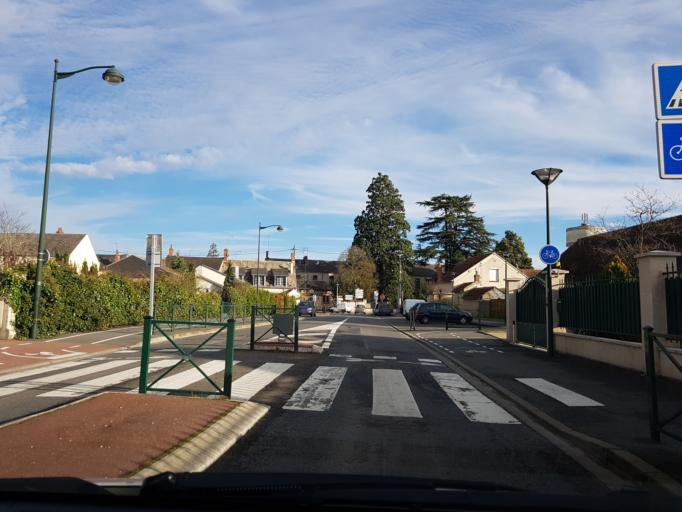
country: FR
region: Centre
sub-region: Departement du Loiret
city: Jargeau
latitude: 47.8631
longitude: 2.1212
